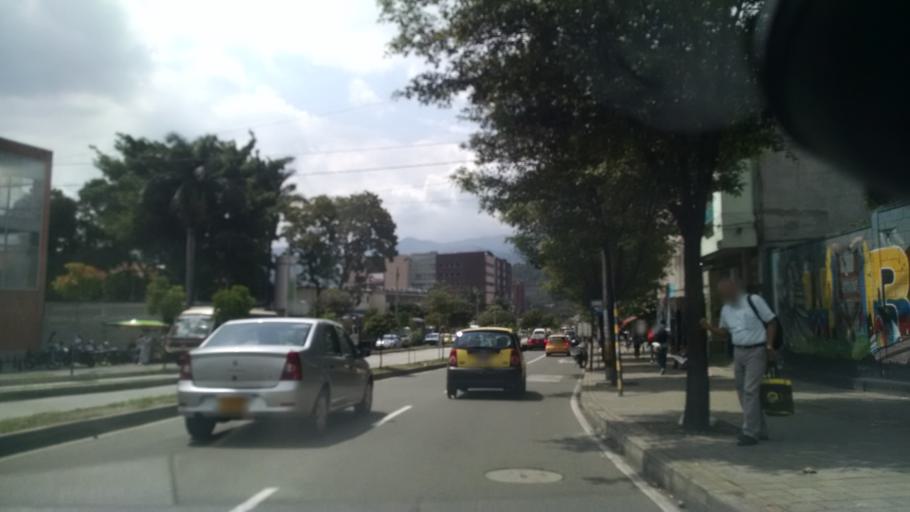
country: CO
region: Antioquia
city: Medellin
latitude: 6.2641
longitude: -75.5641
